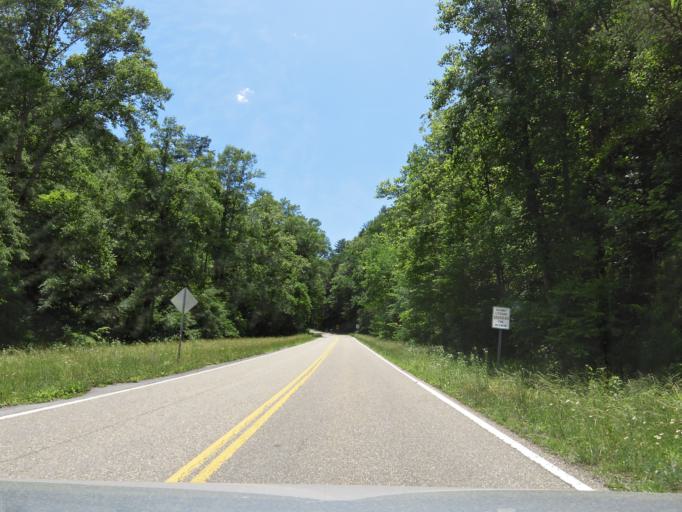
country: US
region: Tennessee
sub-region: Loudon County
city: Greenback
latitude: 35.5234
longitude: -83.9926
